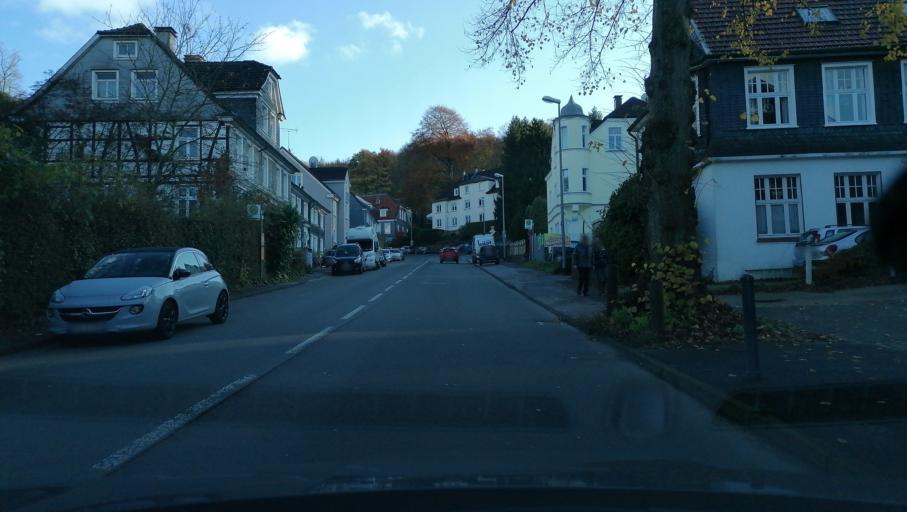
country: DE
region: North Rhine-Westphalia
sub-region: Regierungsbezirk Arnsberg
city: Schwelm
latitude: 51.2802
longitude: 7.2942
